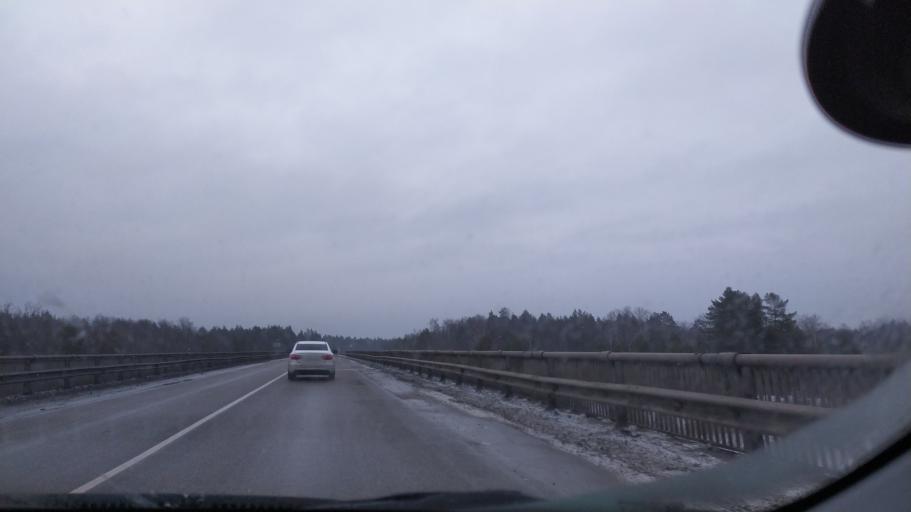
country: RU
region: Chuvashia
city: Mariinskiy Posad
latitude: 56.1922
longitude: 47.7059
